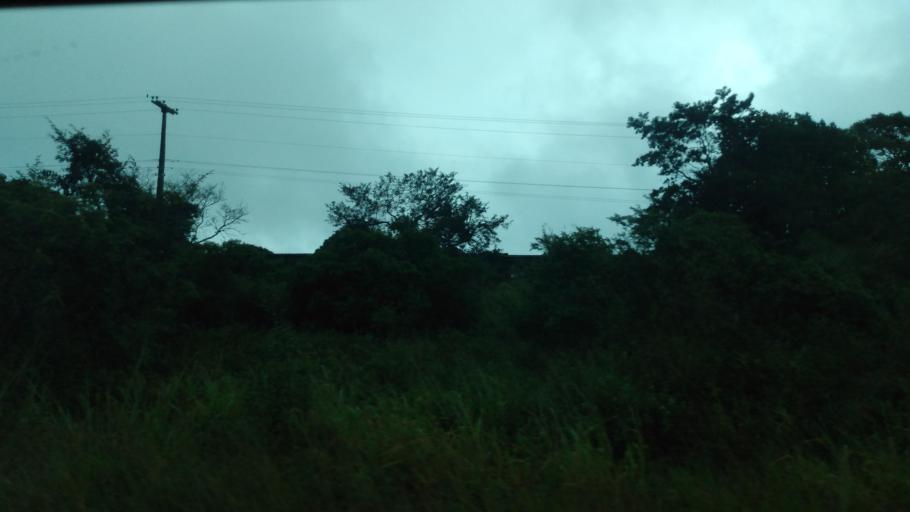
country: BR
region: Pernambuco
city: Garanhuns
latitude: -8.8746
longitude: -36.5290
